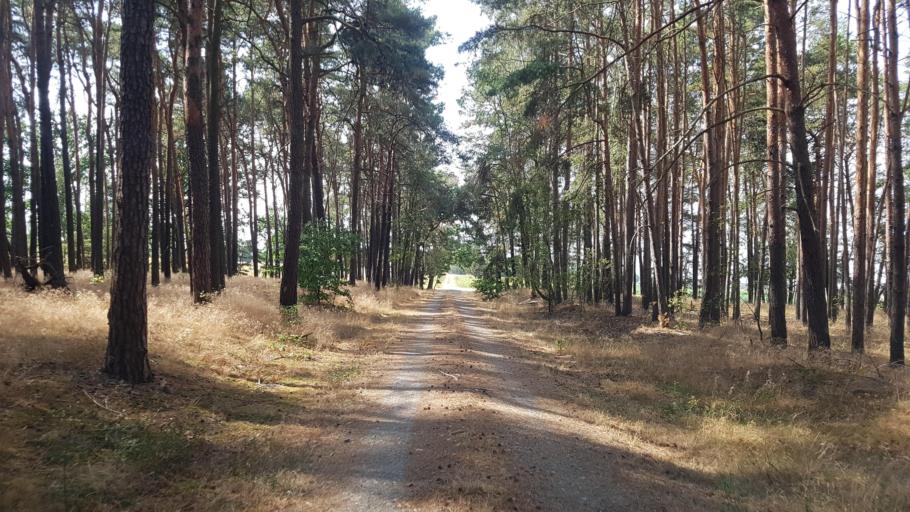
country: DE
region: Brandenburg
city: Finsterwalde
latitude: 51.6528
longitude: 13.7437
